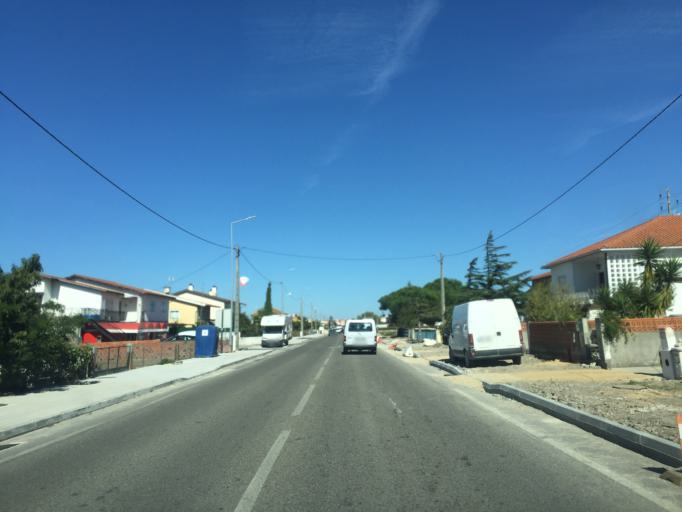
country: PT
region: Coimbra
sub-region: Montemor-O-Velho
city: Arazede
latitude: 40.3075
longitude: -8.7566
